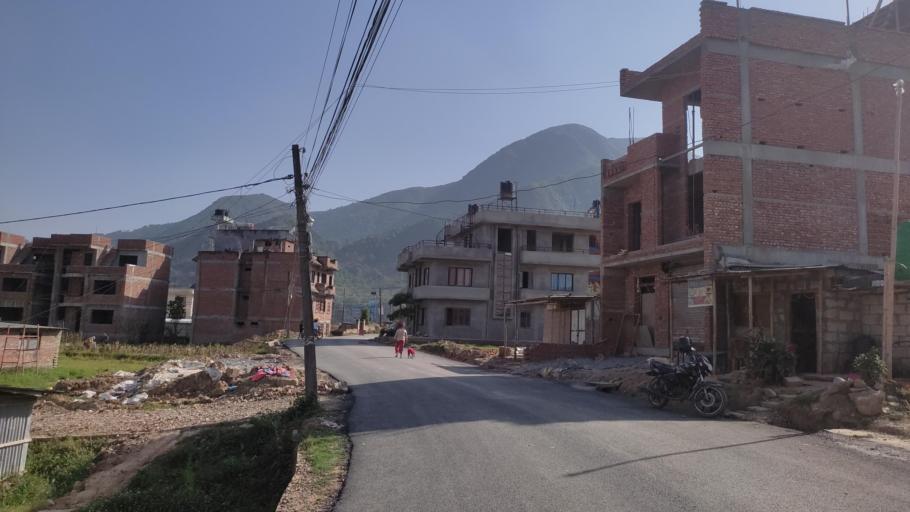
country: NP
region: Central Region
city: Kirtipur
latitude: 27.6668
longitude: 85.2705
